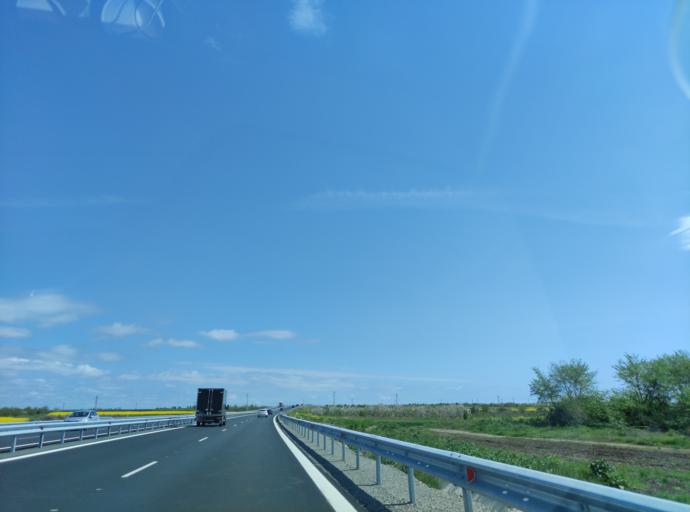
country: BG
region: Burgas
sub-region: Obshtina Pomorie
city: Pomorie
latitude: 42.5749
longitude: 27.5763
